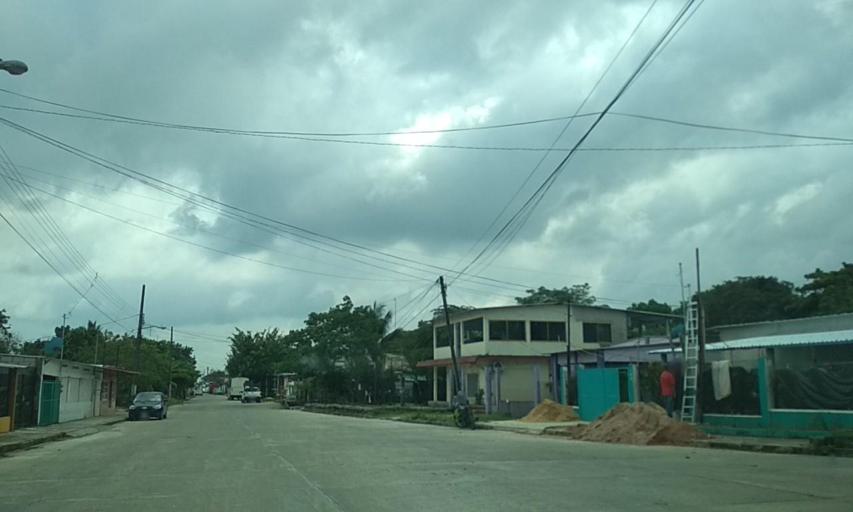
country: MX
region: Veracruz
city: Las Choapas
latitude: 17.9000
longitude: -94.1036
